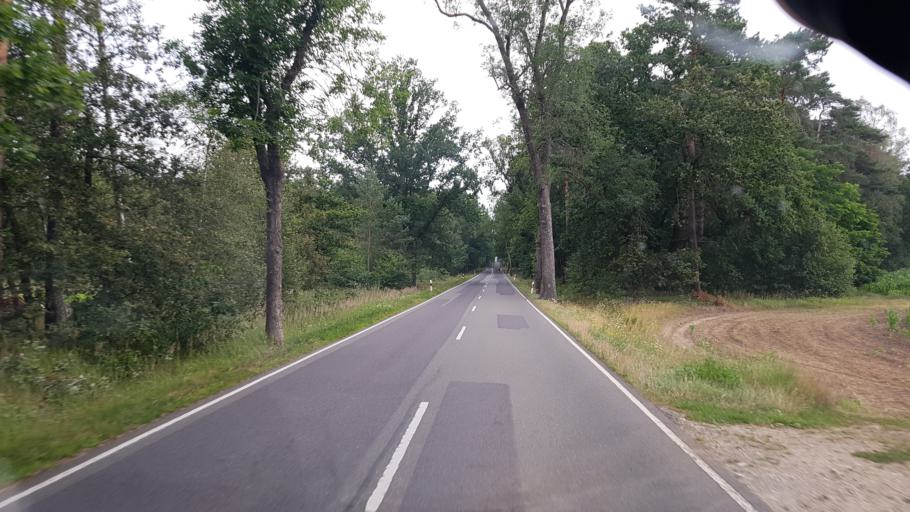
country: DE
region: Brandenburg
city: Lebusa
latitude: 51.8179
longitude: 13.4193
